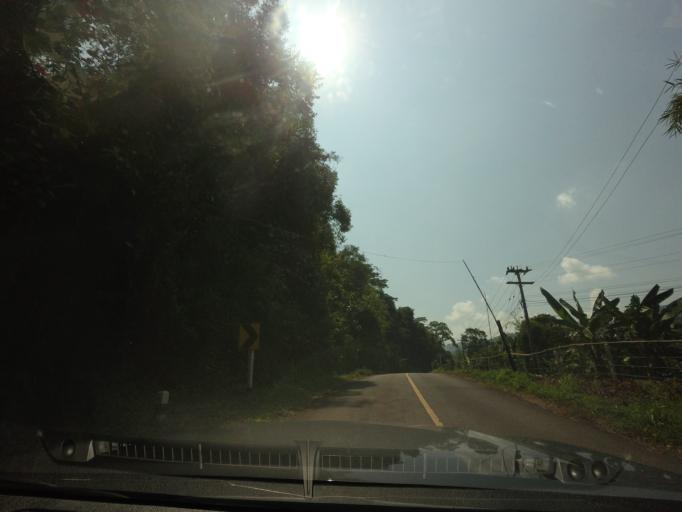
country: TH
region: Nan
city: Bo Kluea
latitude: 19.0354
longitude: 101.1734
